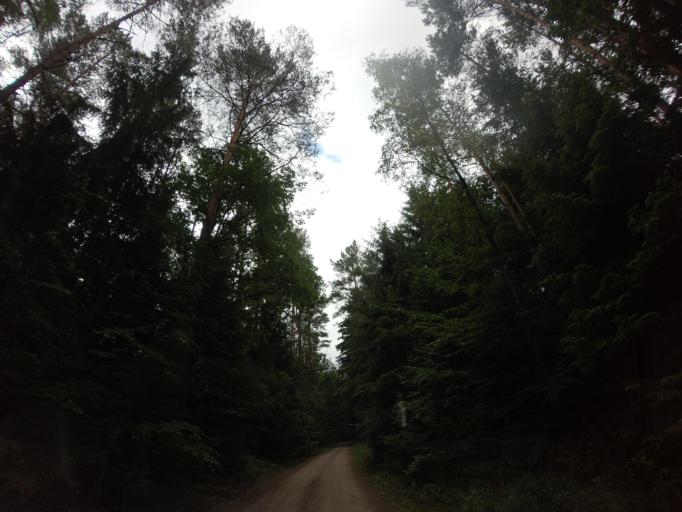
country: PL
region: Lubusz
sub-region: Powiat strzelecko-drezdenecki
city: Strzelce Krajenskie
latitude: 52.9328
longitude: 15.6105
